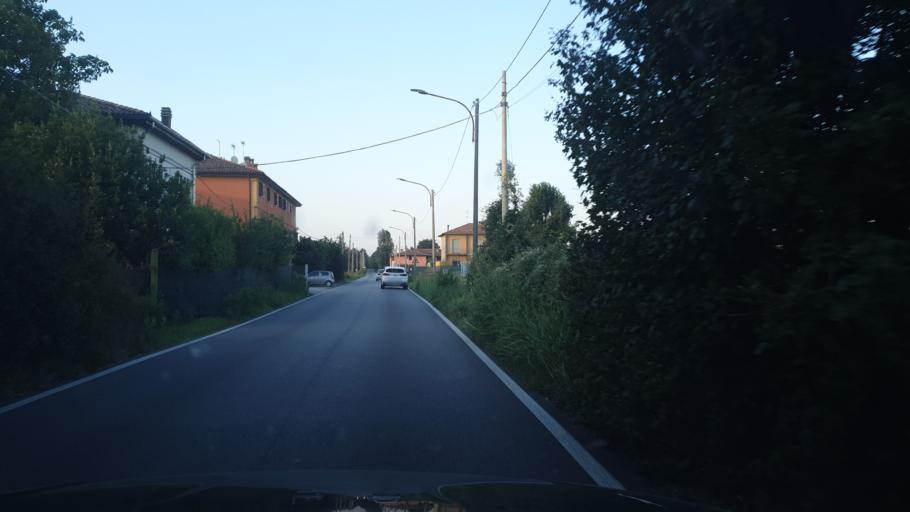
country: IT
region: Emilia-Romagna
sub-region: Provincia di Bologna
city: Quarto Inferiore
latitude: 44.5370
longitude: 11.3917
